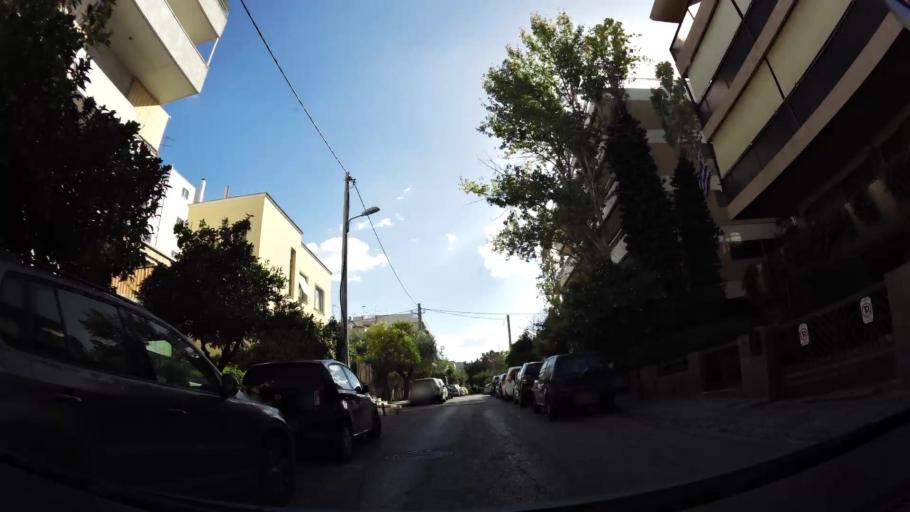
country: GR
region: Attica
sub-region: Nomarchia Athinas
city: Neo Psychiko
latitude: 38.0047
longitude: 23.7778
